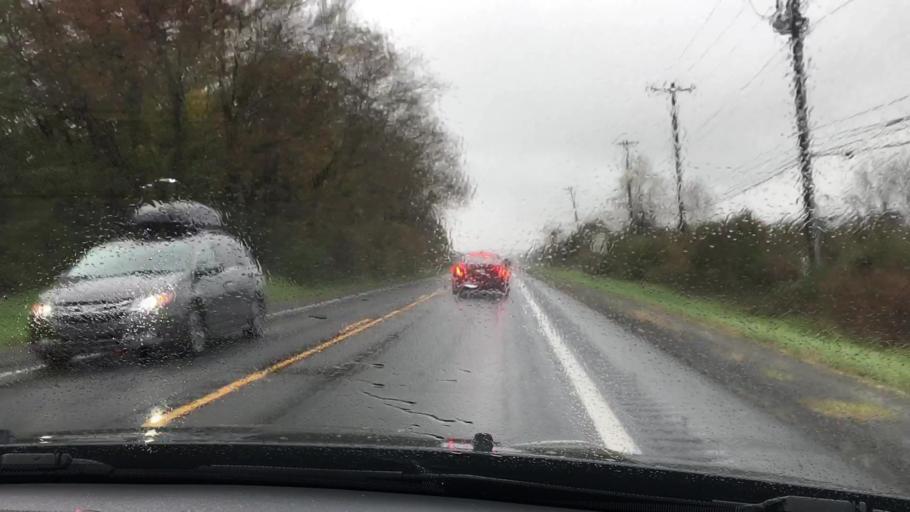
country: US
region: Virginia
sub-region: Loudoun County
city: Leesburg
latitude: 39.1563
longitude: -77.5389
